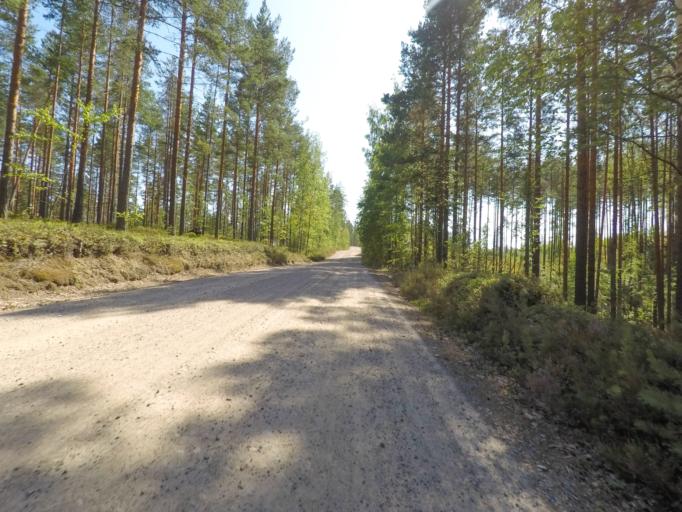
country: FI
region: Southern Savonia
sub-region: Mikkeli
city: Puumala
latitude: 61.4220
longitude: 28.0417
